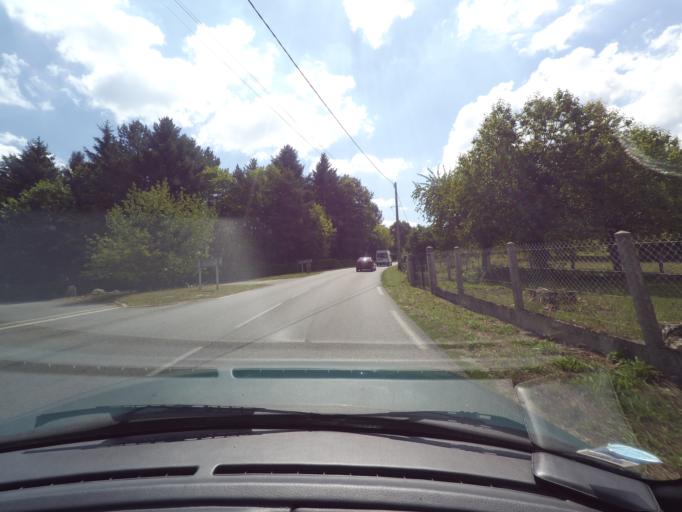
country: FR
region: Limousin
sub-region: Departement de la Haute-Vienne
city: Limoges
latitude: 45.8023
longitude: 1.2536
